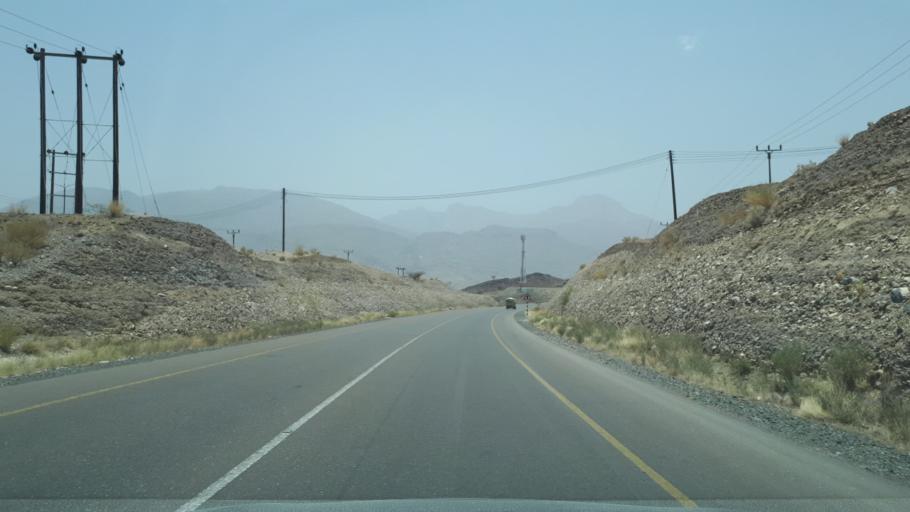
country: OM
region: Al Batinah
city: Rustaq
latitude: 23.4178
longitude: 57.2623
